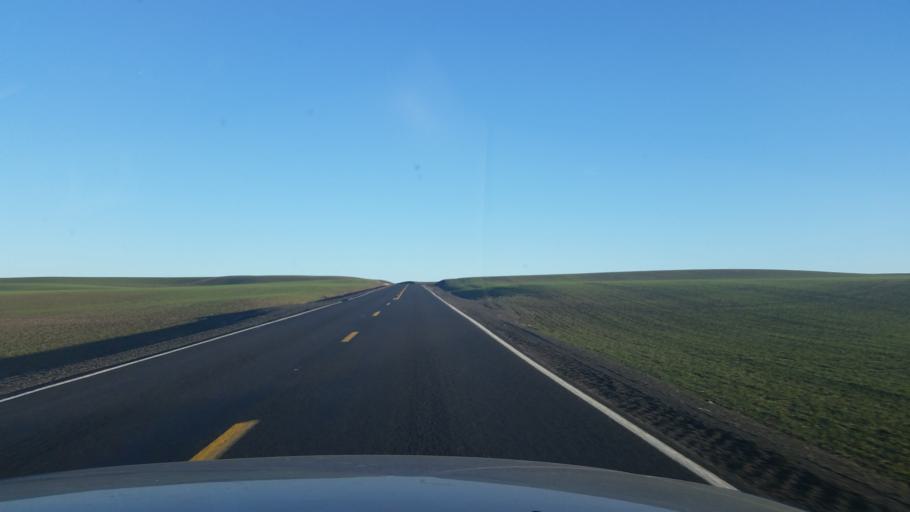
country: US
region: Washington
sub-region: Spokane County
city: Opportunity
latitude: 47.3611
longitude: -117.2800
